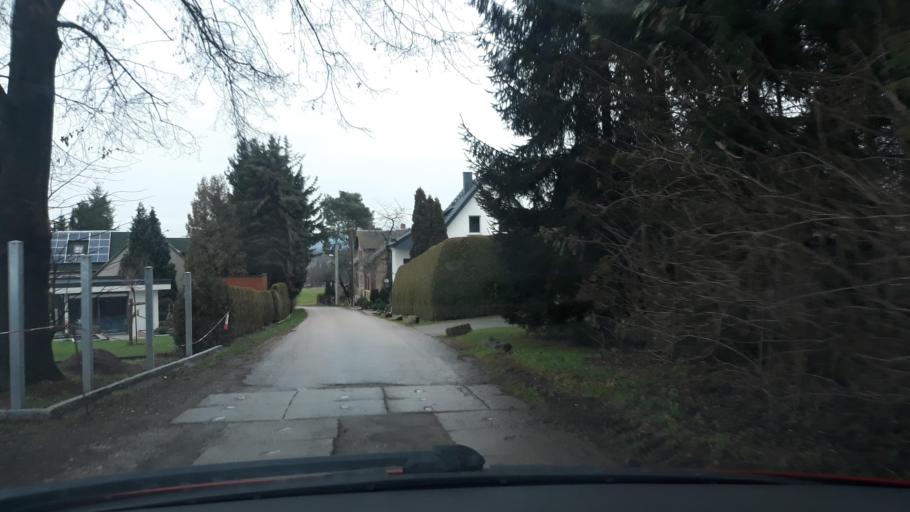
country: DE
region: Saxony
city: Kirchberg
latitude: 50.6502
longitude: 12.5469
